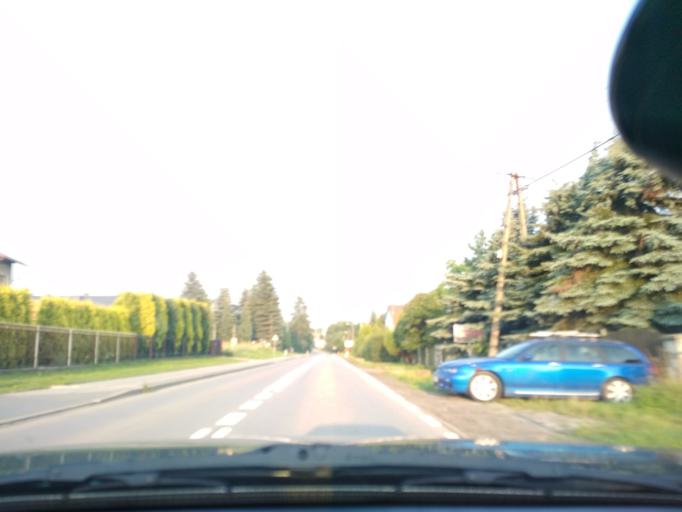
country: PL
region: Lesser Poland Voivodeship
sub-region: Powiat olkuski
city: Wolbrom
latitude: 50.3923
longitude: 19.7472
